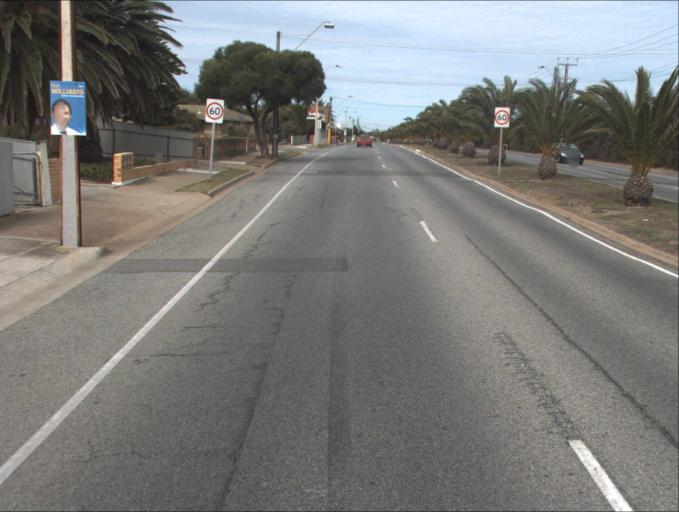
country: AU
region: South Australia
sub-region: Charles Sturt
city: West Lakes Shore
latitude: -34.8594
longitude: 138.4789
